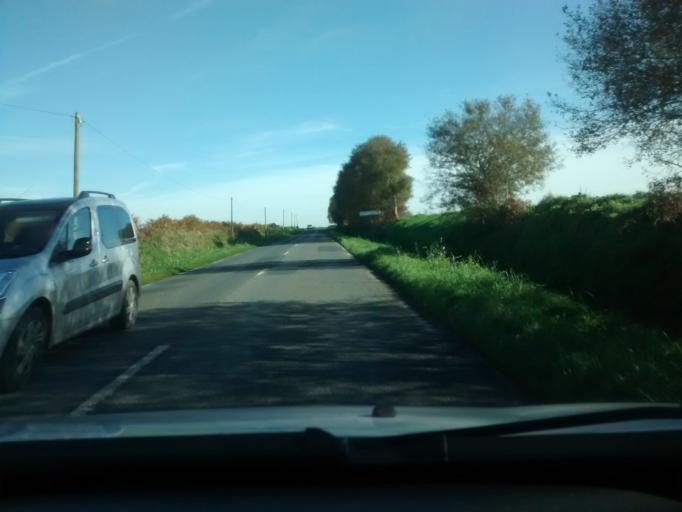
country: FR
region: Brittany
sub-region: Departement des Cotes-d'Armor
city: Langoat
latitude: 48.7674
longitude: -3.2760
